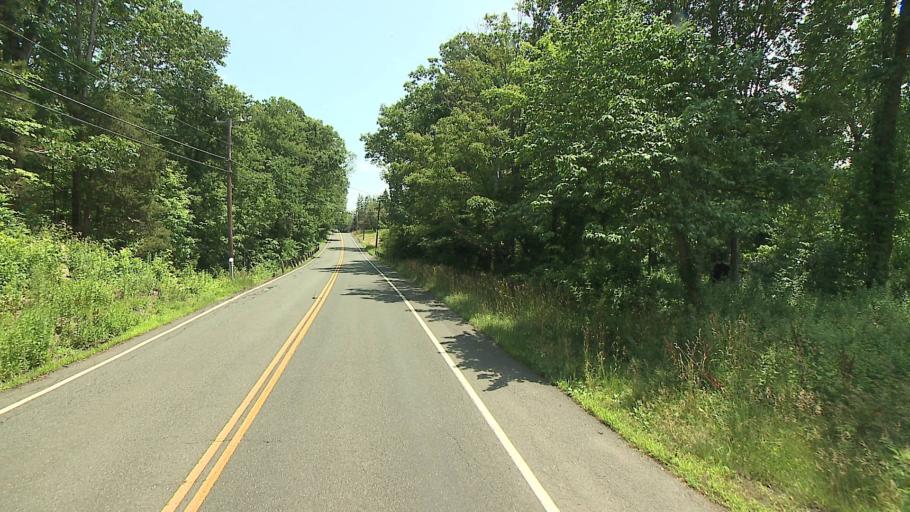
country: US
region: Connecticut
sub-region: Hartford County
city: Tariffville
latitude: 41.9179
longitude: -72.7445
